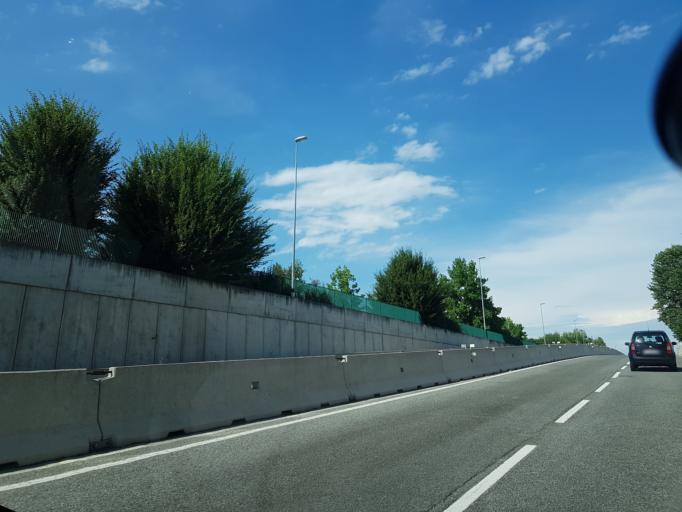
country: IT
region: Piedmont
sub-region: Provincia di Cuneo
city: Cuneo
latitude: 44.3901
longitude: 7.5838
